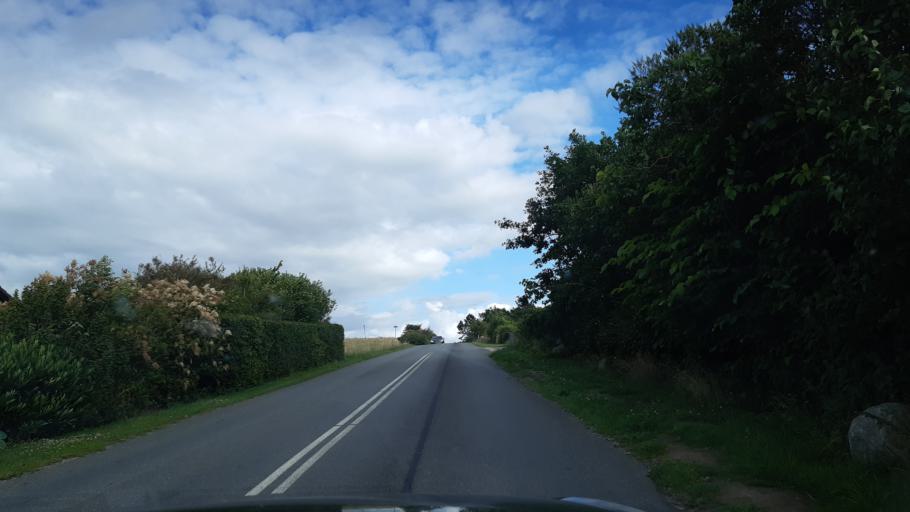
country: DK
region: Zealand
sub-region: Odsherred Kommune
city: Horve
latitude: 55.8175
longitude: 11.4156
